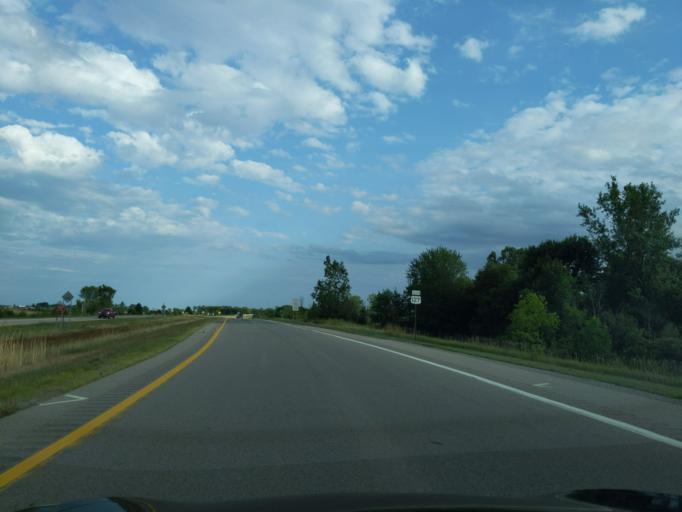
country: US
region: Michigan
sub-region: Clare County
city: Clare
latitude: 43.8081
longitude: -84.7668
